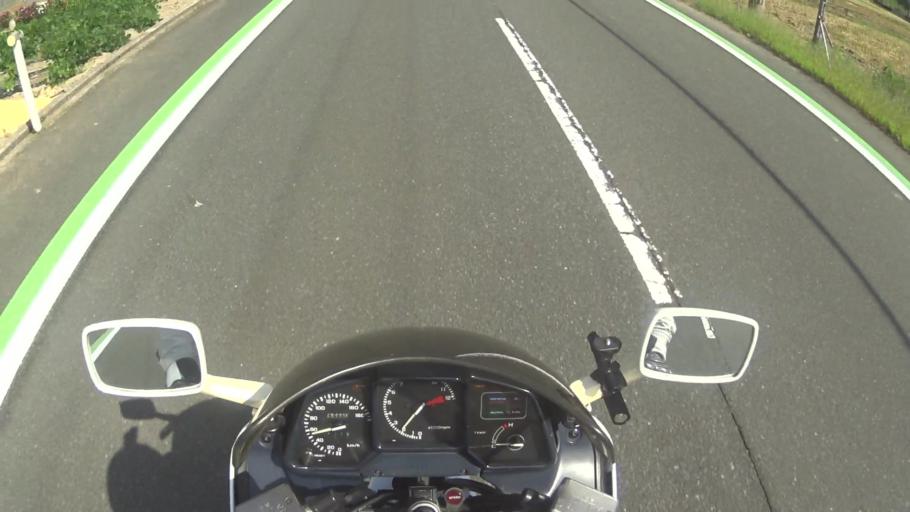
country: JP
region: Kyoto
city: Miyazu
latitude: 35.7300
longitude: 135.2587
